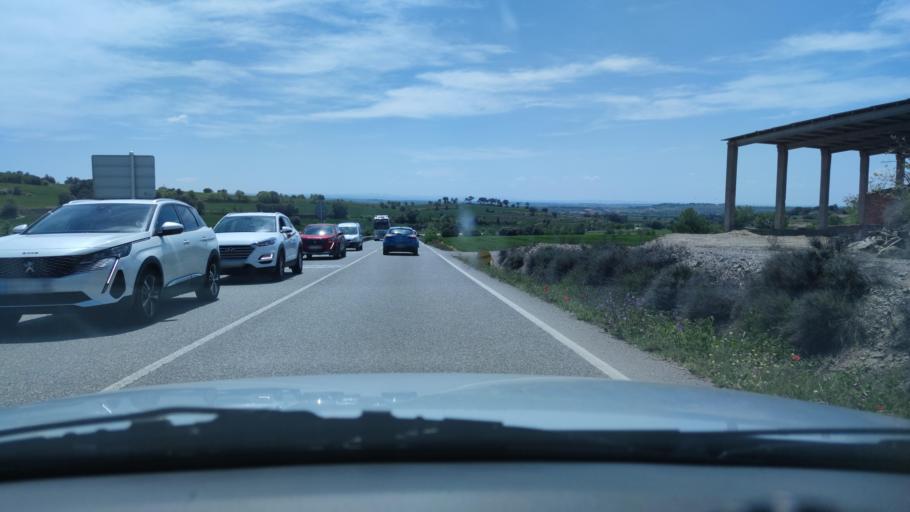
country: ES
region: Catalonia
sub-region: Provincia de Lleida
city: Mont-roig del Camp
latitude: 41.7660
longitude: 1.2519
